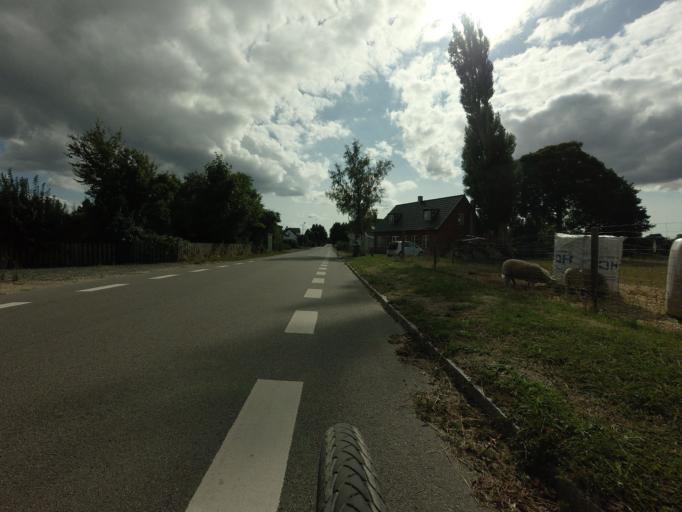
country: DK
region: Zealand
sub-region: Vordingborg Kommune
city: Stege
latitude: 55.0022
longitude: 12.3143
